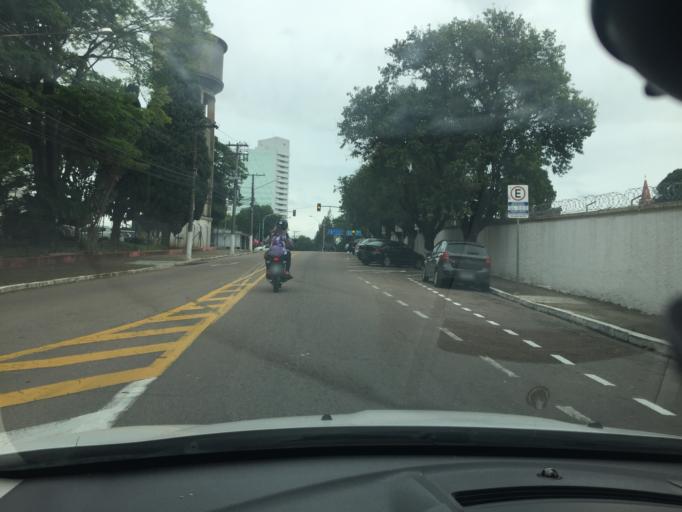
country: BR
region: Sao Paulo
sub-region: Jundiai
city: Jundiai
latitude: -23.1805
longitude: -46.8908
